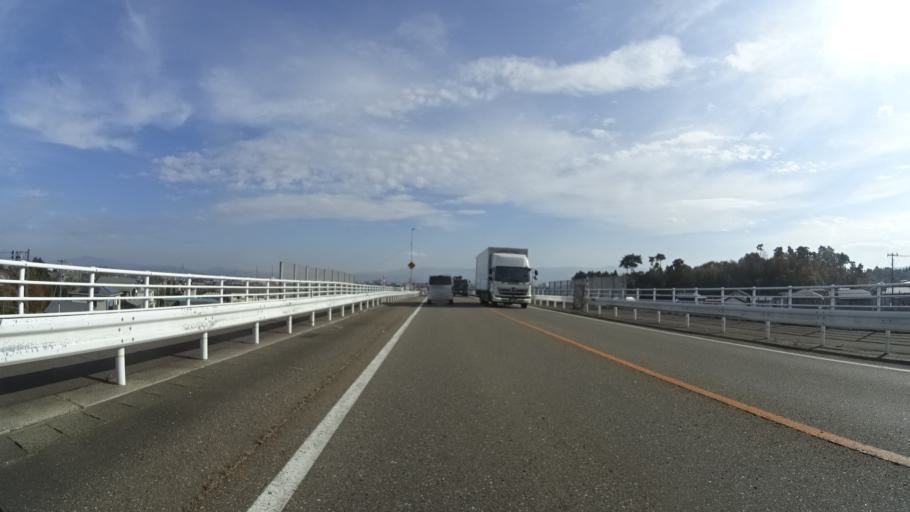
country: JP
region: Niigata
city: Joetsu
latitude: 37.1614
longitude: 138.2203
